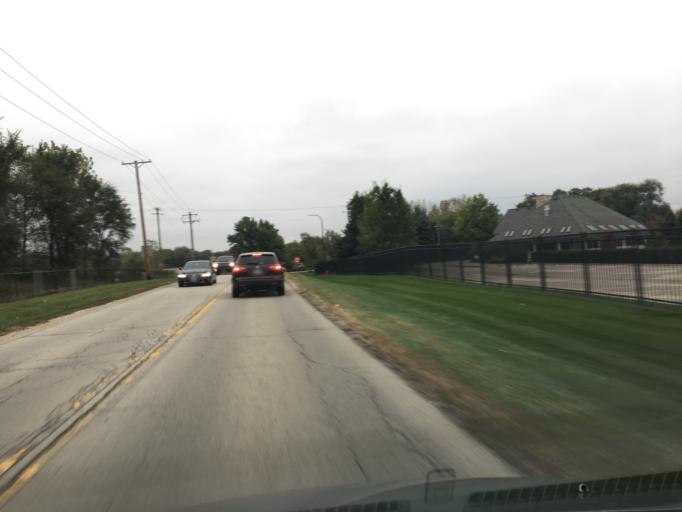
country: US
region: Illinois
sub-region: Will County
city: Plainfield
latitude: 41.6392
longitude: -88.1645
